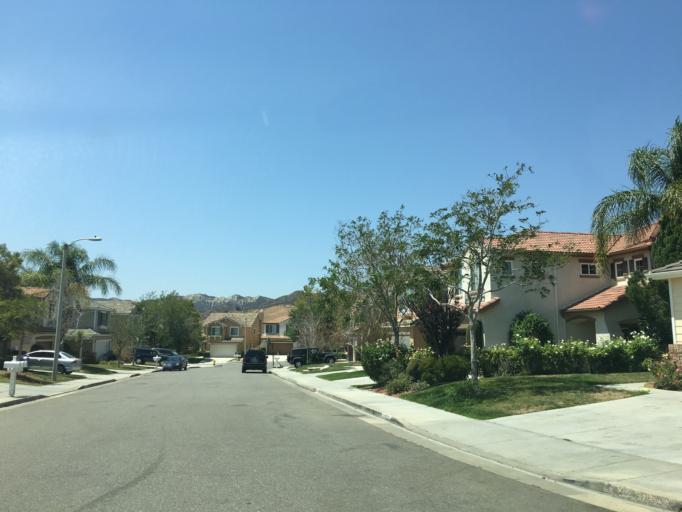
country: US
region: California
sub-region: Los Angeles County
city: Castaic
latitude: 34.5033
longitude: -118.6208
